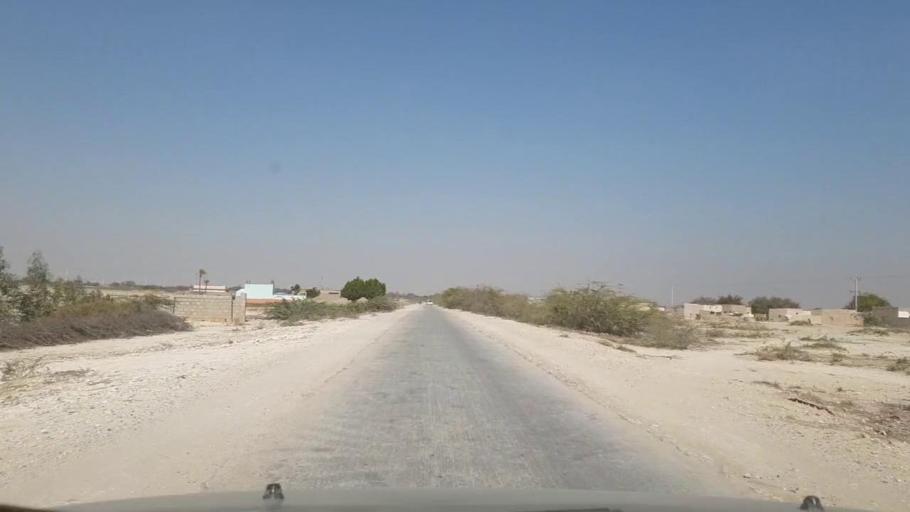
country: PK
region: Sindh
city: Daro Mehar
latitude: 25.0074
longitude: 68.0143
